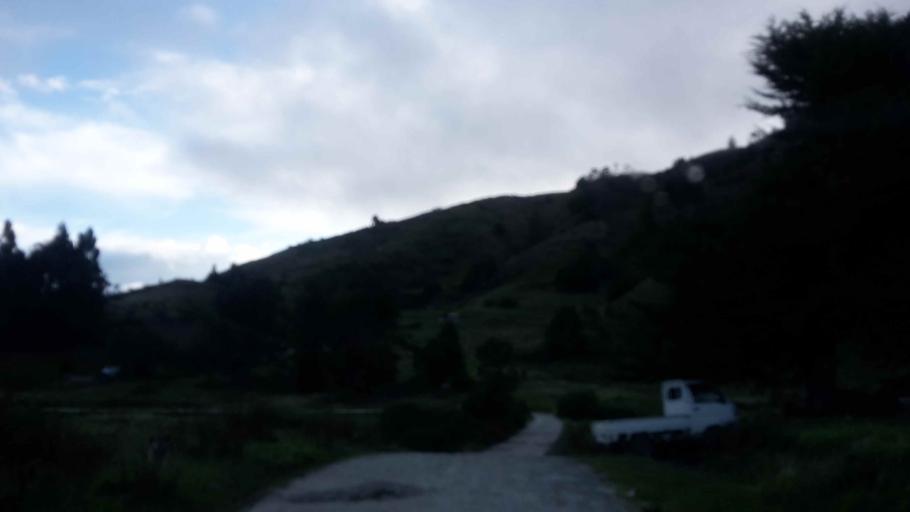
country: BO
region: Cochabamba
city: Colomi
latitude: -17.2623
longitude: -65.9059
